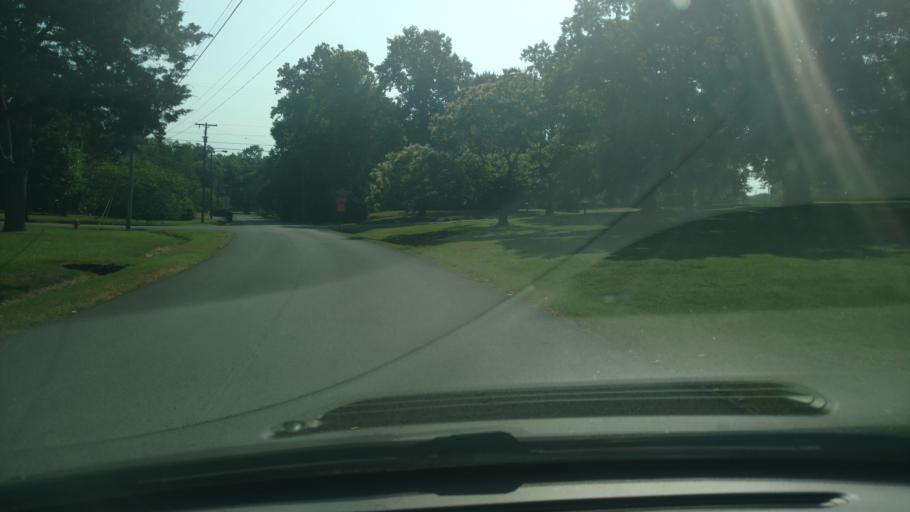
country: US
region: Tennessee
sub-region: Davidson County
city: Lakewood
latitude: 36.2244
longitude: -86.7194
